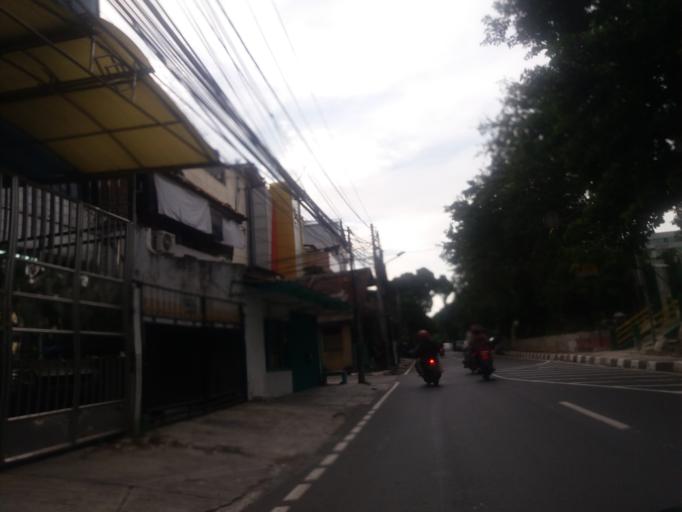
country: ID
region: Jakarta Raya
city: Jakarta
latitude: -6.1572
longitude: 106.8364
